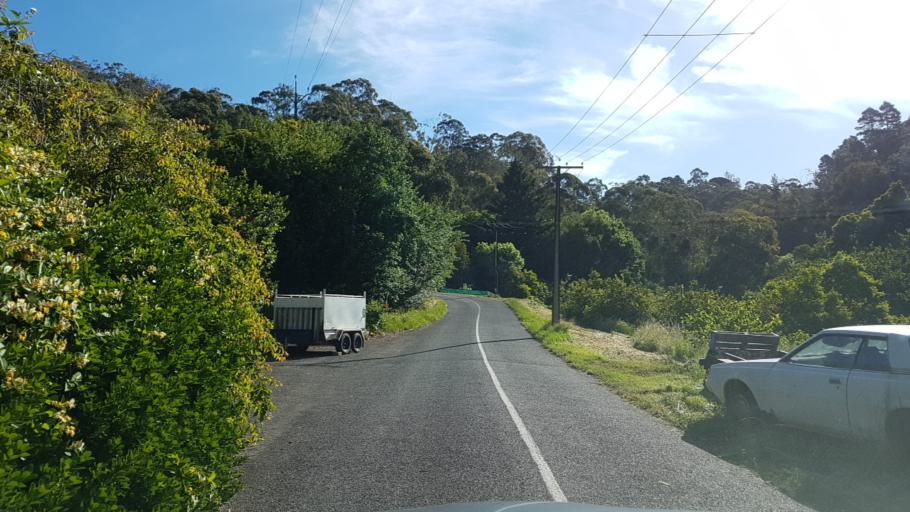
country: AU
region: South Australia
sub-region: Adelaide Hills
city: Adelaide Hills
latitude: -34.9092
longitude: 138.7730
